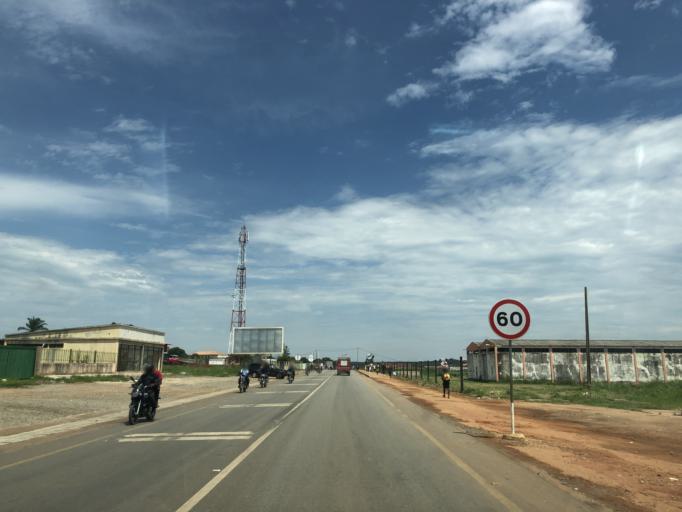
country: AO
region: Cuanza Sul
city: Quibala
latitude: -10.7352
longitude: 14.9820
